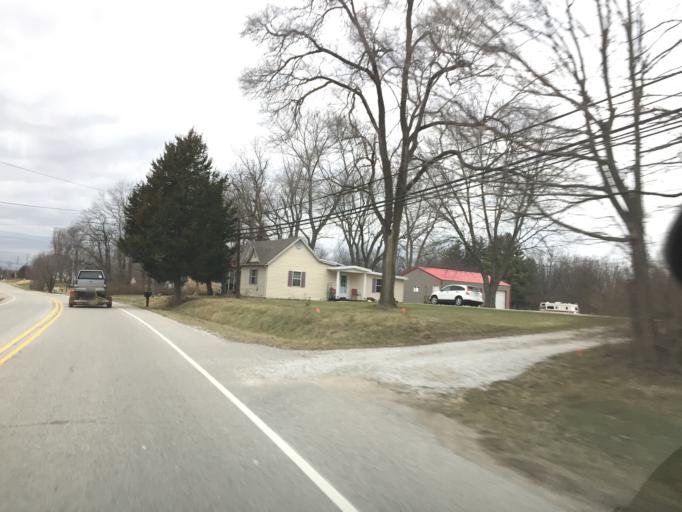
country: US
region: Indiana
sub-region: Monroe County
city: Ellettsville
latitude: 39.2078
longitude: -86.5742
